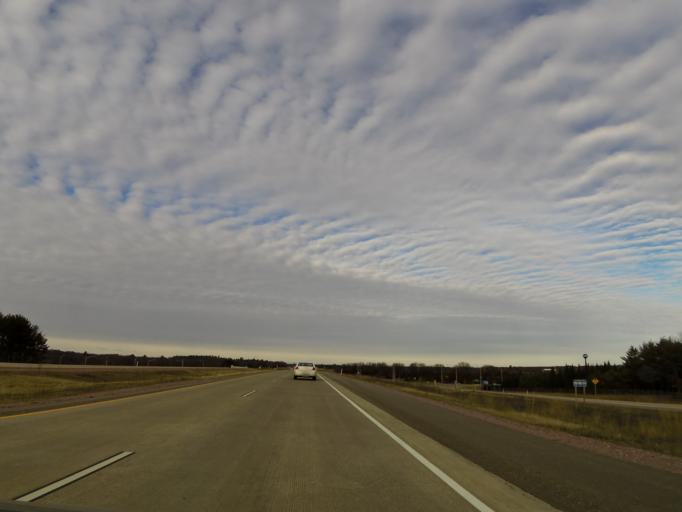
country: US
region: Wisconsin
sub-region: Sauk County
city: West Baraboo
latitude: 43.5300
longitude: -89.7870
